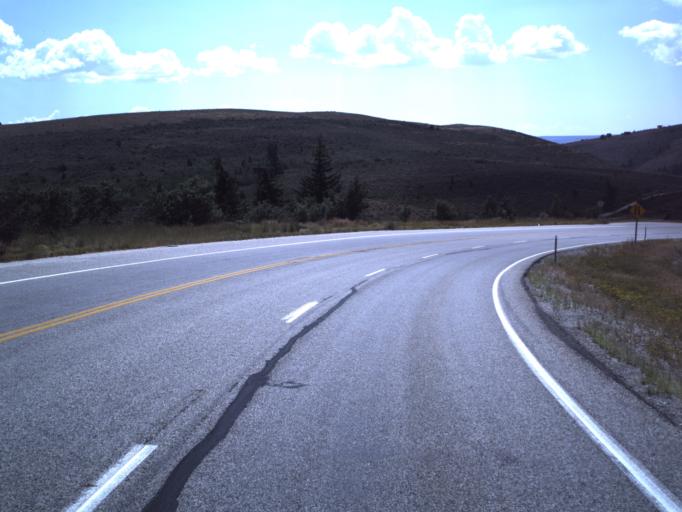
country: US
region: Idaho
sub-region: Bear Lake County
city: Paris
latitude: 41.9256
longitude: -111.4303
